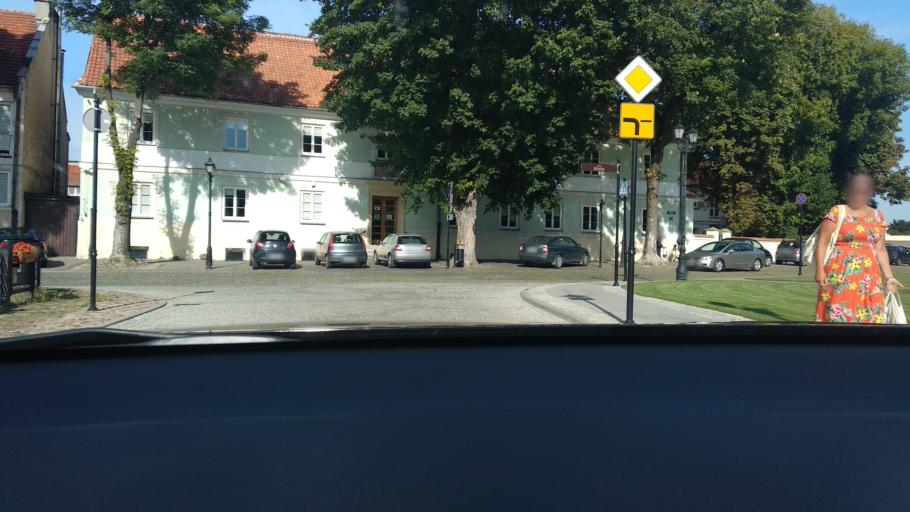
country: PL
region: Masovian Voivodeship
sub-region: Powiat pultuski
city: Pultusk
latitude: 52.7047
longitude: 21.0928
